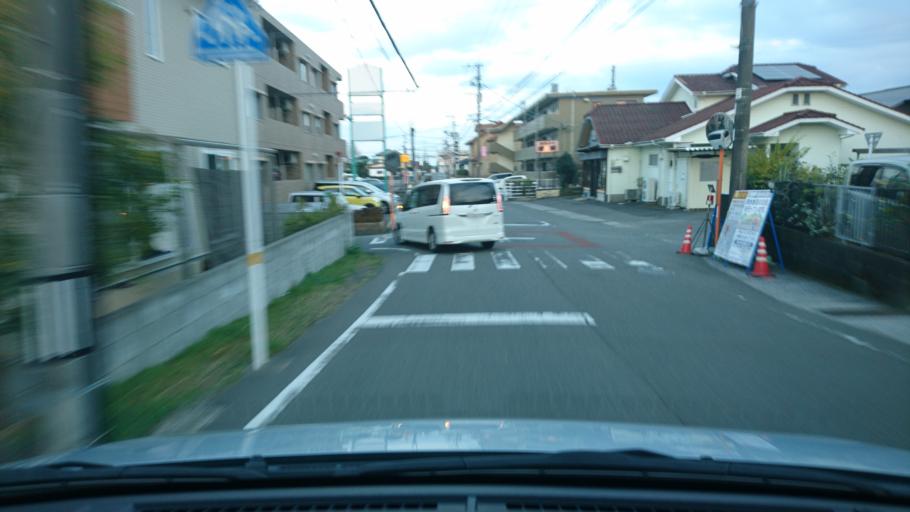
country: JP
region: Miyazaki
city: Miyazaki-shi
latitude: 31.8606
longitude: 131.4308
